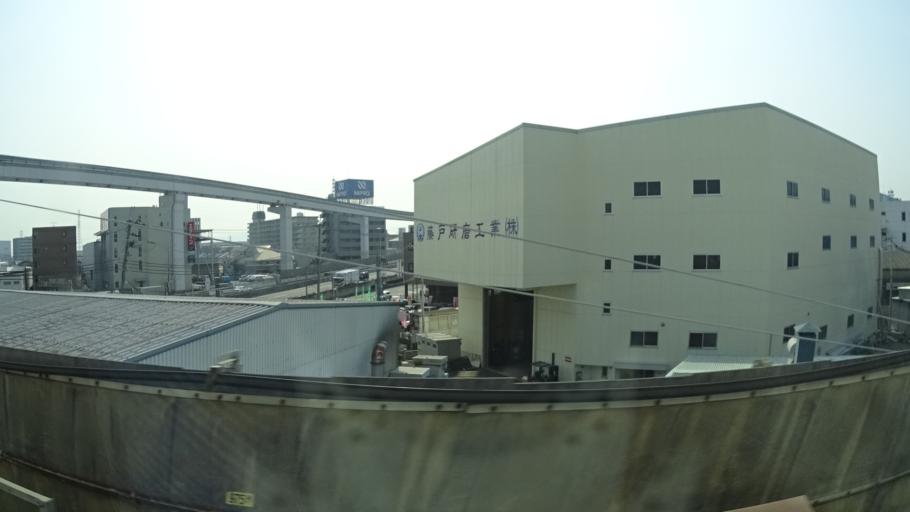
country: JP
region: Osaka
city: Kadoma
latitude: 34.7702
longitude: 135.5649
